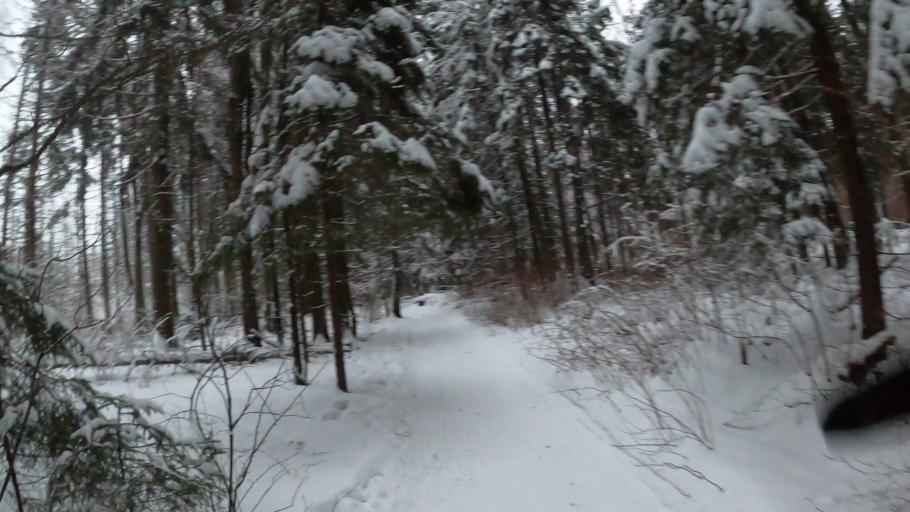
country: RU
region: Moskovskaya
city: Firsanovka
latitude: 55.9066
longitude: 37.2040
